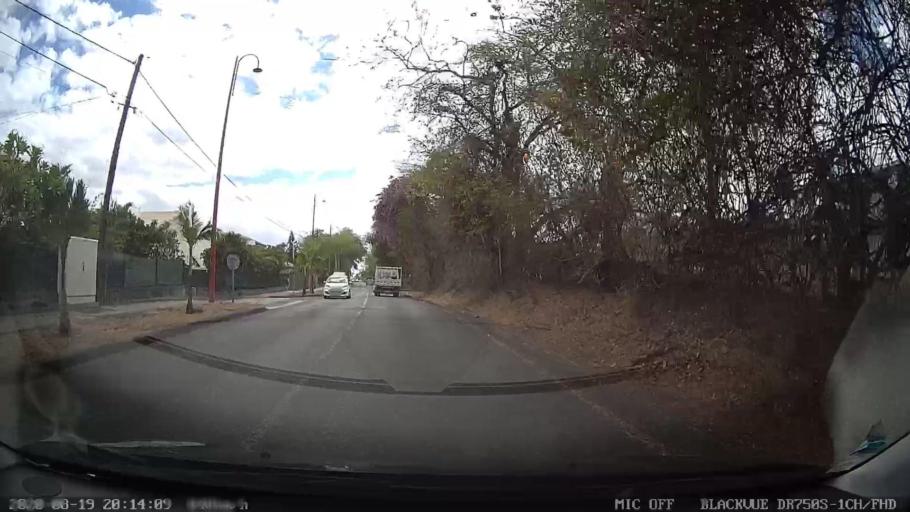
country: RE
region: Reunion
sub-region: Reunion
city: La Possession
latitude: -20.9349
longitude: 55.3340
